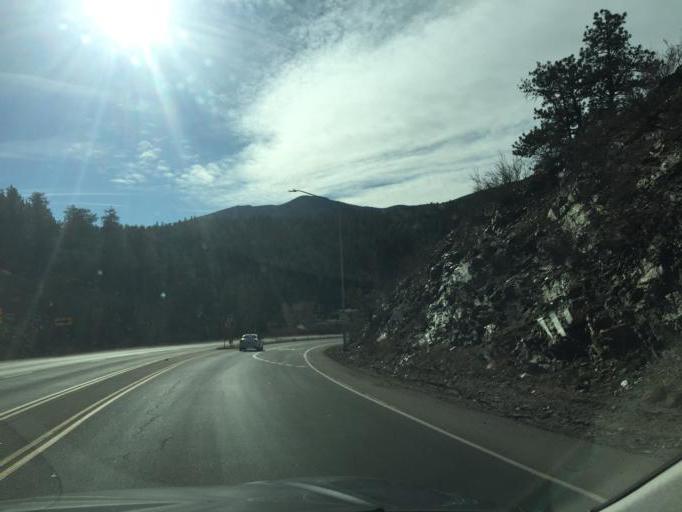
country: US
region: Colorado
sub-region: Jefferson County
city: Evergreen
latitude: 39.4078
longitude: -105.4730
